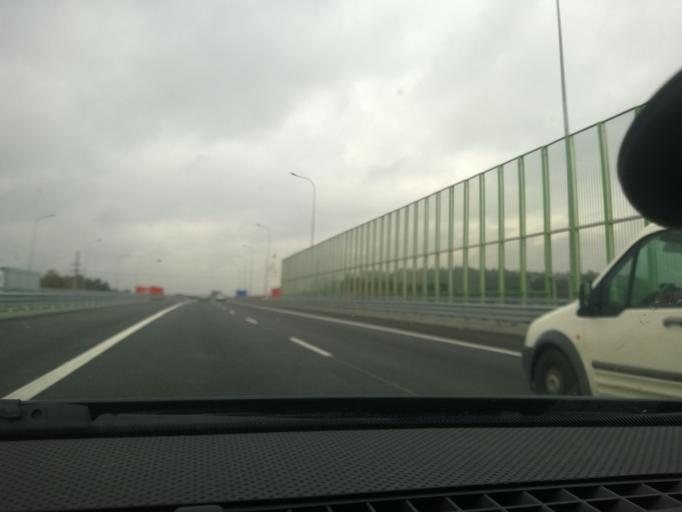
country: PL
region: Lodz Voivodeship
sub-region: Powiat lodzki wschodni
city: Andrespol
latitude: 51.7522
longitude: 19.5958
